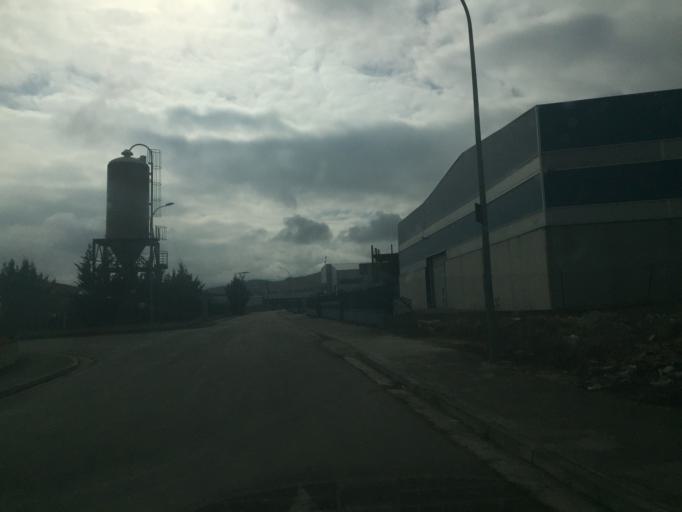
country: ES
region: Castille and Leon
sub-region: Provincia de Burgos
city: Medina de Pomar
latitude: 42.9257
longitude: -3.5812
